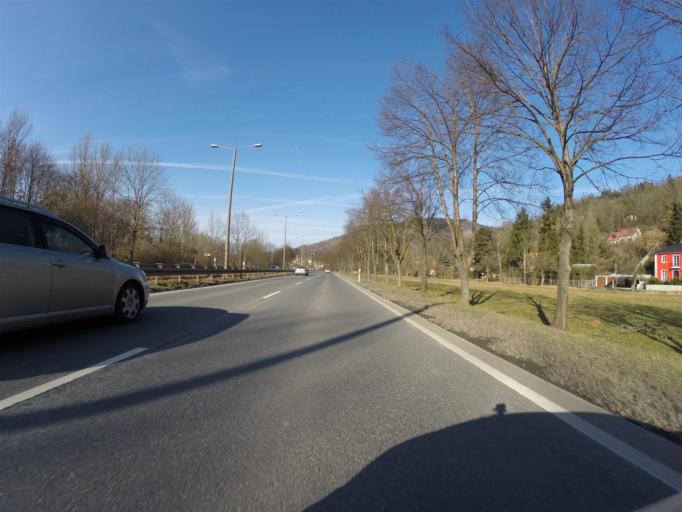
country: DE
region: Thuringia
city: Jena
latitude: 50.8996
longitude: 11.6002
